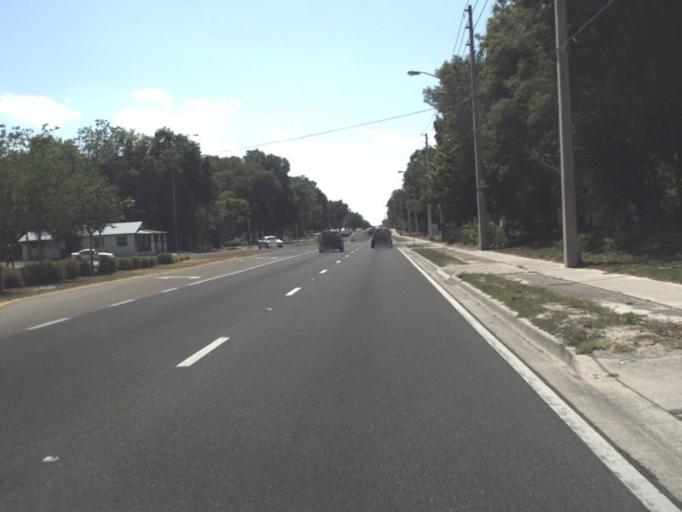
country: US
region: Florida
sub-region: Marion County
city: Ocala
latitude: 29.1863
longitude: -82.1593
